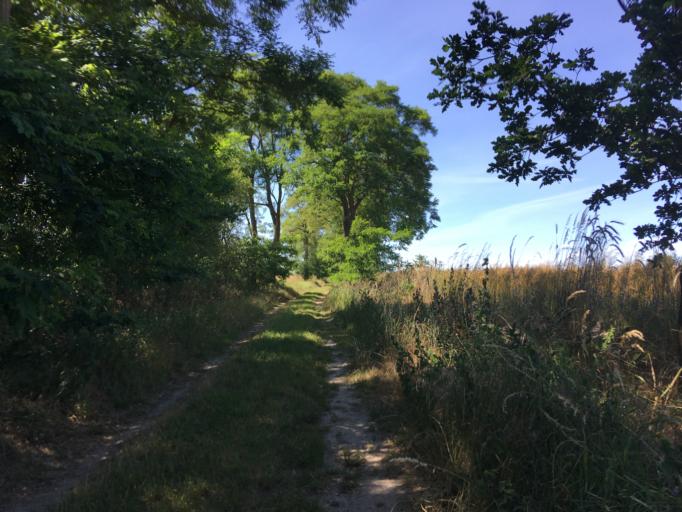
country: DE
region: Brandenburg
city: Brussow
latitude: 53.3292
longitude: 14.0743
